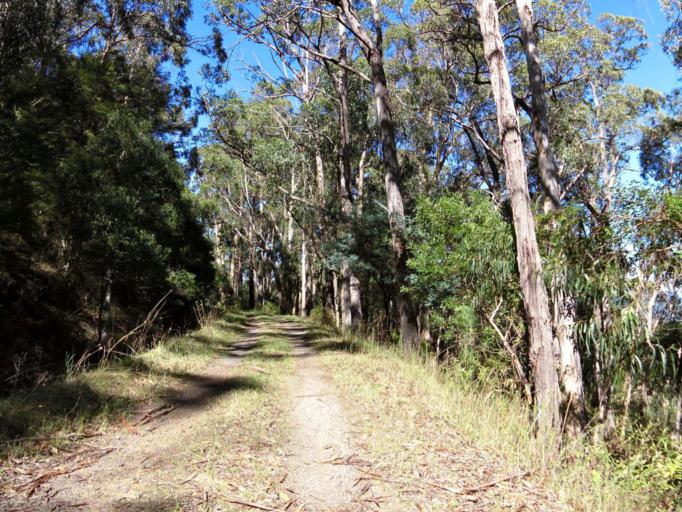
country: AU
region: Victoria
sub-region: Yarra Ranges
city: Yarra Junction
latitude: -37.7404
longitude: 145.5968
